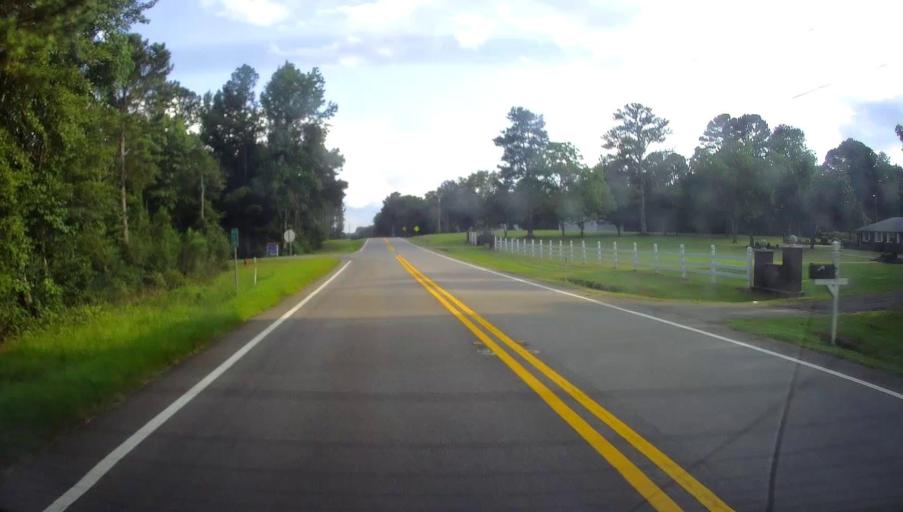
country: US
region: Georgia
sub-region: Monroe County
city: Forsyth
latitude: 32.9795
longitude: -83.9528
